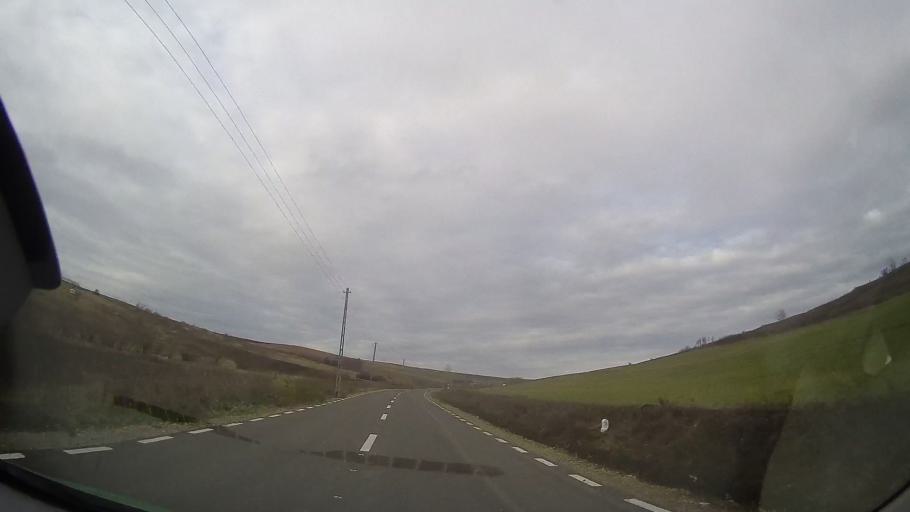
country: RO
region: Mures
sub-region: Comuna Cozma
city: Cozma
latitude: 46.8171
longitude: 24.4915
